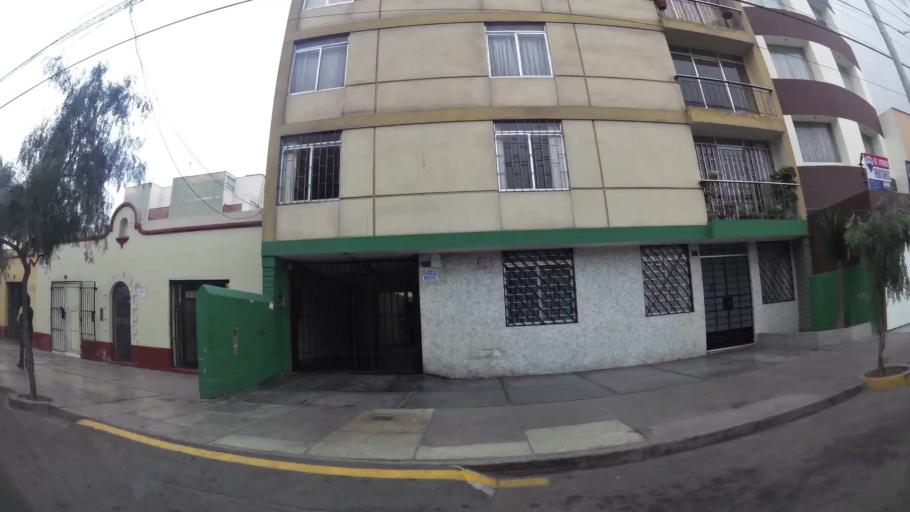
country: PE
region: Lima
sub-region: Lima
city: San Isidro
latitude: -12.1171
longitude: -77.0407
